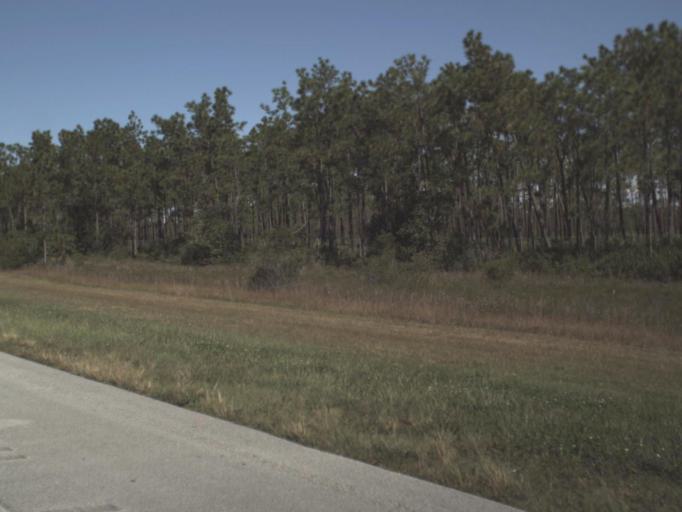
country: US
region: Florida
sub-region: Osceola County
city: Saint Cloud
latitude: 27.9852
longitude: -81.1231
